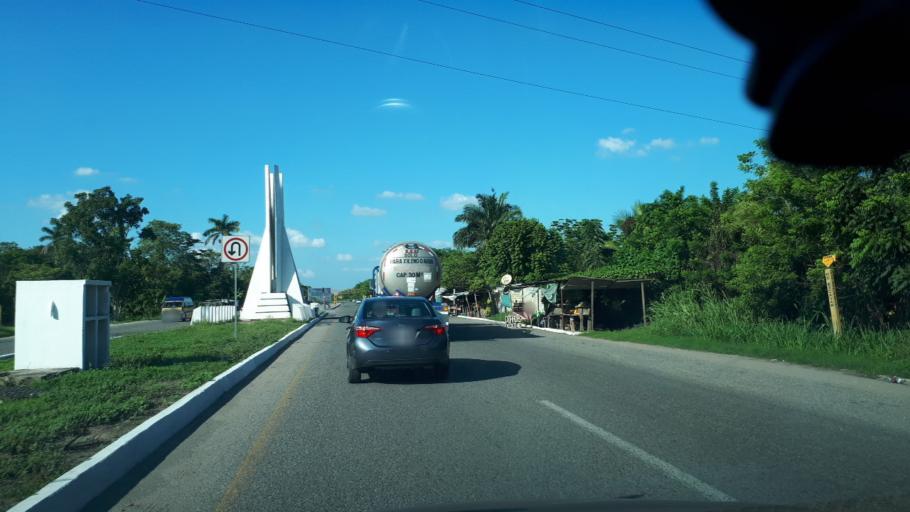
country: MX
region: Tabasco
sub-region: Cunduacan
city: Cumuapa 1ra. Seccion
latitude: 17.9753
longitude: -93.1290
